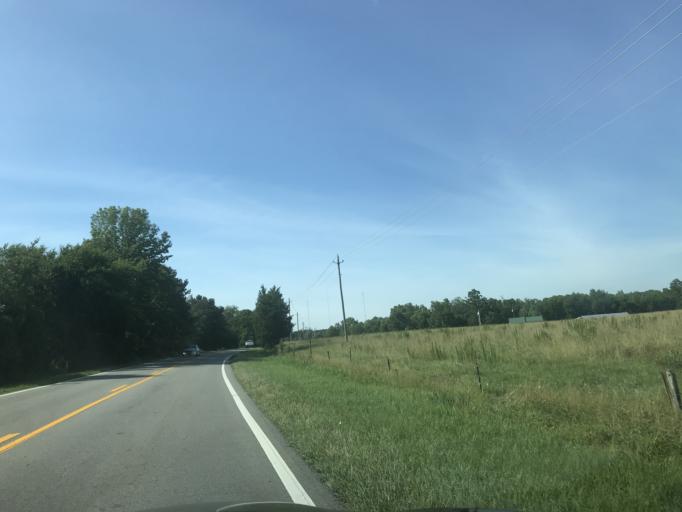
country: US
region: North Carolina
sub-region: Johnston County
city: Clayton
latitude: 35.6115
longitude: -78.5354
